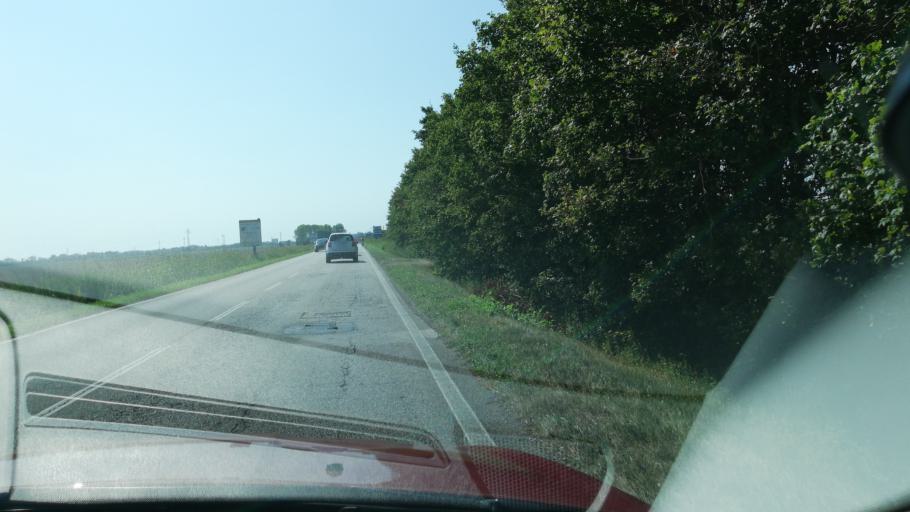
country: IT
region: Veneto
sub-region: Provincia di Venezia
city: Caorle
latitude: 45.6209
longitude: 12.8670
